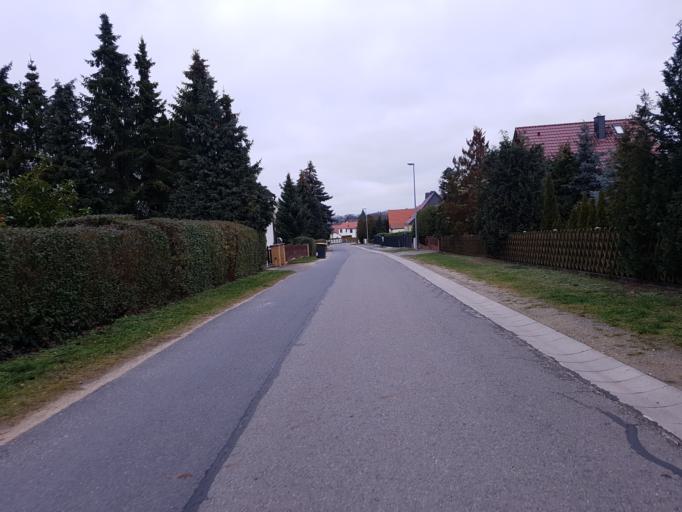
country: DE
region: Brandenburg
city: Groden
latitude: 51.4036
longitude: 13.5775
